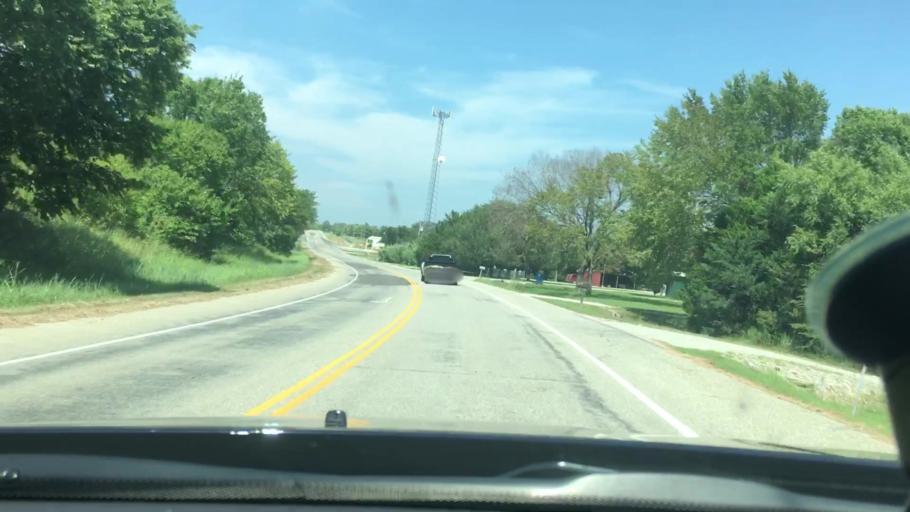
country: US
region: Oklahoma
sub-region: Pontotoc County
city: Byng
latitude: 34.8650
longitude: -96.6688
